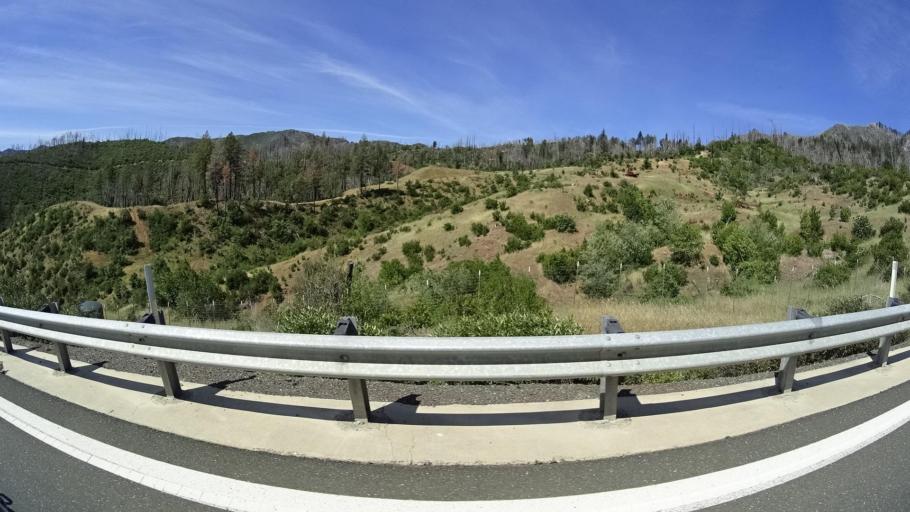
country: US
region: California
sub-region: Lake County
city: Cobb
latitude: 38.7944
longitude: -122.7035
